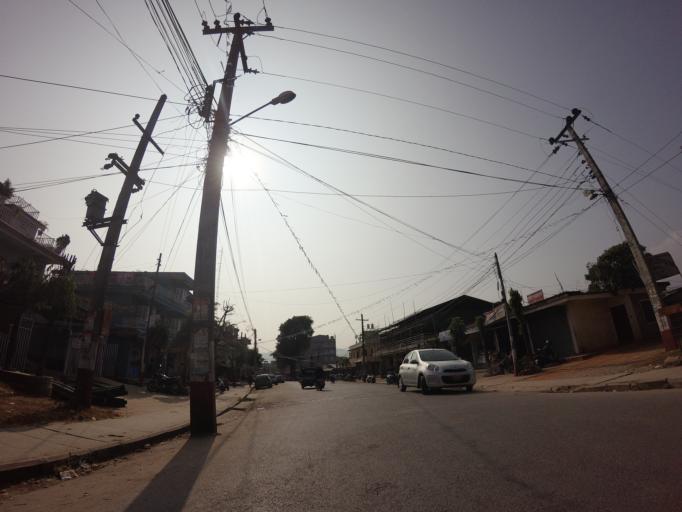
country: NP
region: Western Region
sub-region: Gandaki Zone
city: Pokhara
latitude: 28.2130
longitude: 83.9814
